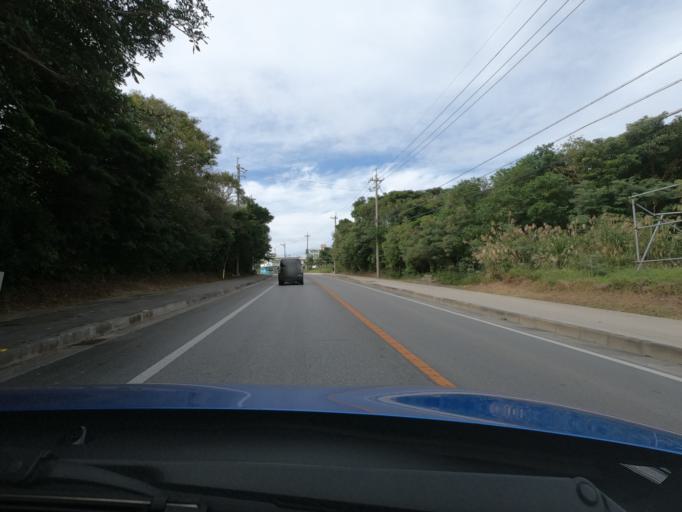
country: JP
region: Okinawa
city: Nago
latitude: 26.6800
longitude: 127.8869
